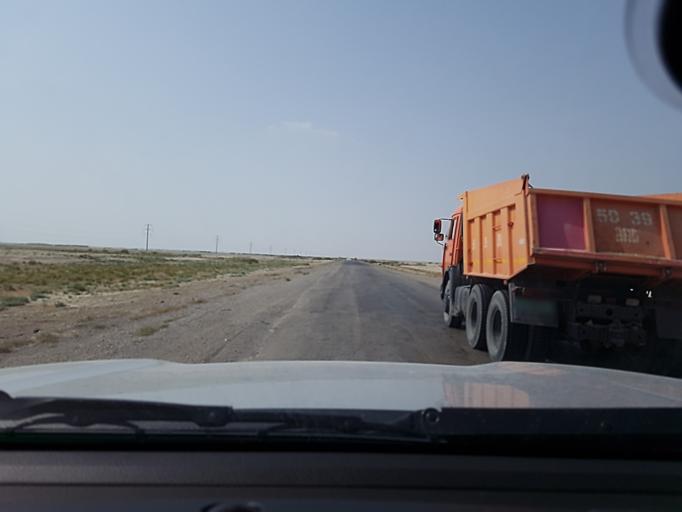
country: TM
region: Balkan
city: Gumdag
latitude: 38.9140
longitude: 54.5915
